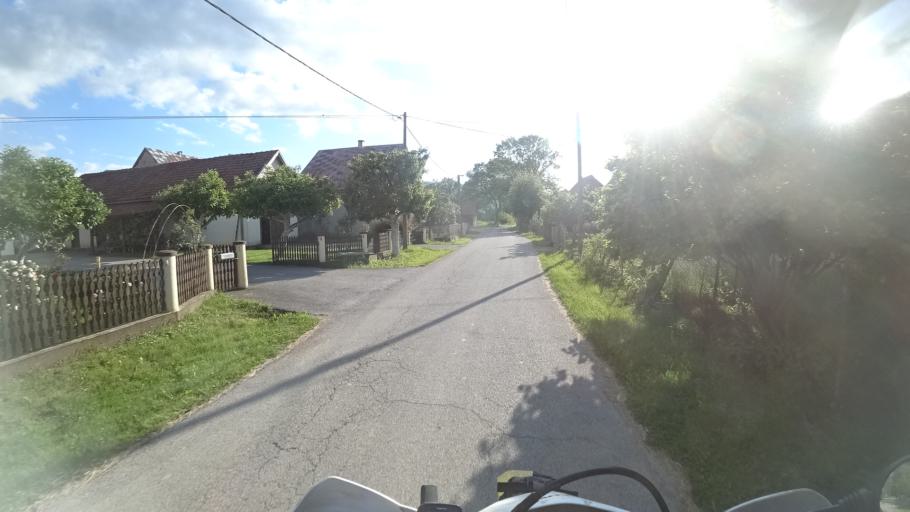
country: HR
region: Licko-Senjska
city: Gospic
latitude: 44.5120
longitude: 15.3181
